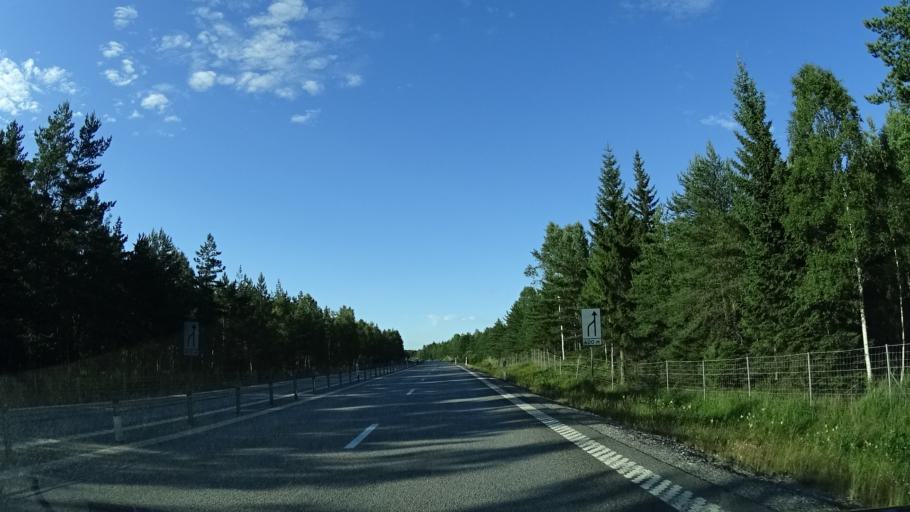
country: SE
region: Stockholm
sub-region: Osterakers Kommun
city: Akersberga
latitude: 59.5985
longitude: 18.2729
